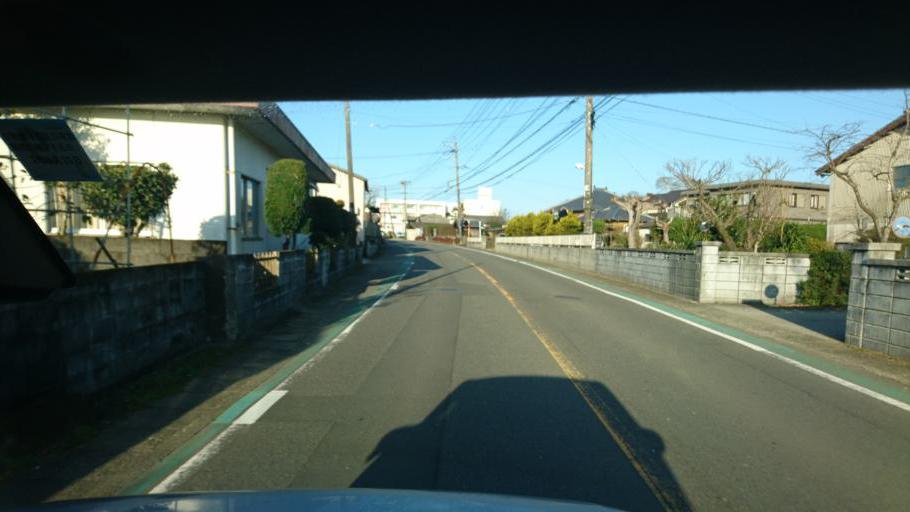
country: JP
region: Miyazaki
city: Miyazaki-shi
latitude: 31.8436
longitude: 131.4057
